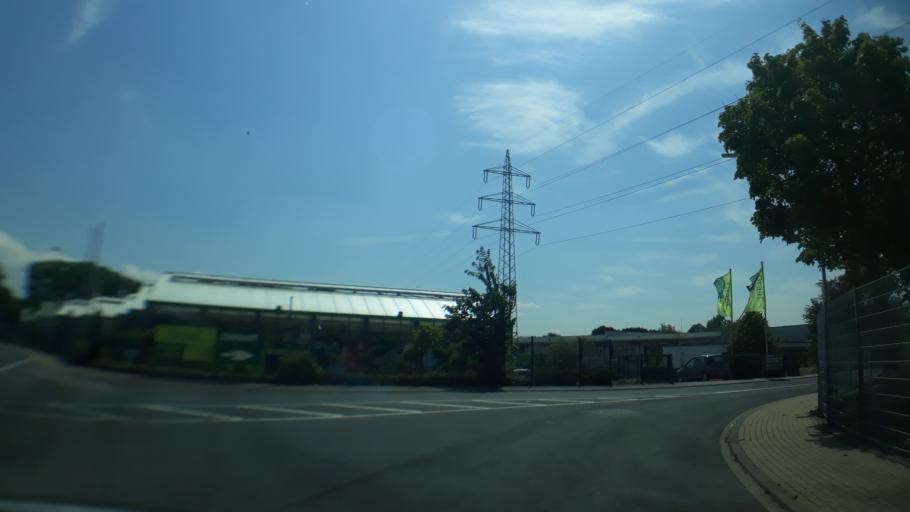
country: DE
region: North Rhine-Westphalia
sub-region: Regierungsbezirk Koln
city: Eschweiler
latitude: 50.8182
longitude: 6.2917
